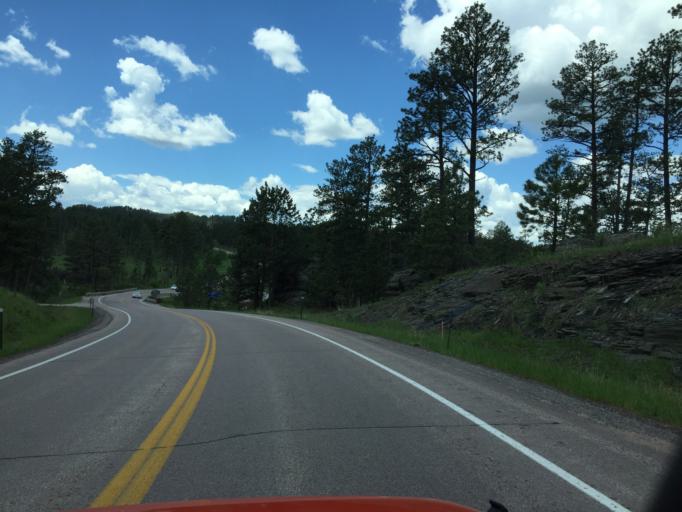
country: US
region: South Dakota
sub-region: Custer County
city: Custer
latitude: 43.9013
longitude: -103.5342
